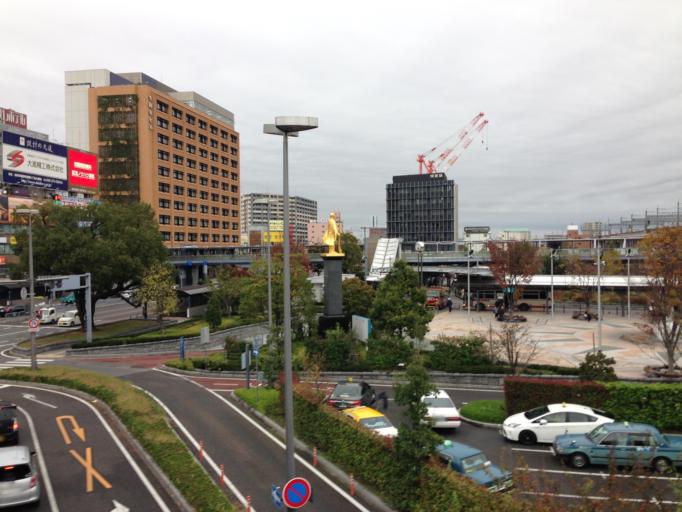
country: JP
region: Gifu
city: Gifu-shi
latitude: 35.4103
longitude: 136.7564
